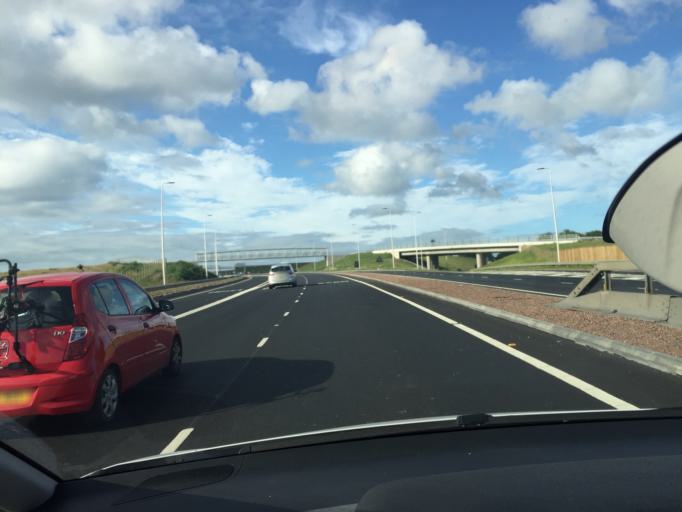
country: GB
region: Scotland
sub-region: North Lanarkshire
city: Bellshill
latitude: 55.8349
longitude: -4.0268
